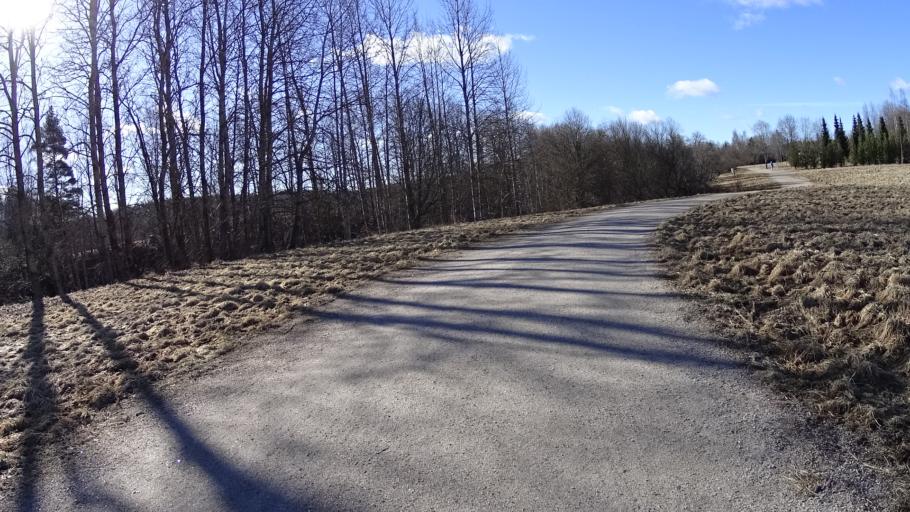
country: FI
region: Uusimaa
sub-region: Helsinki
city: Teekkarikylae
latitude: 60.2760
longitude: 24.8827
